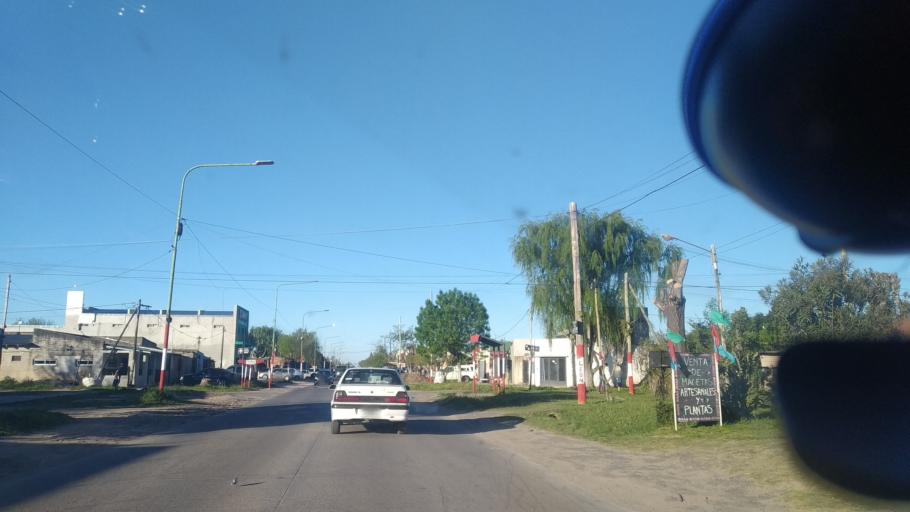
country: AR
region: Buenos Aires
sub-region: Partido de La Plata
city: La Plata
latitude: -34.9636
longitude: -57.9636
